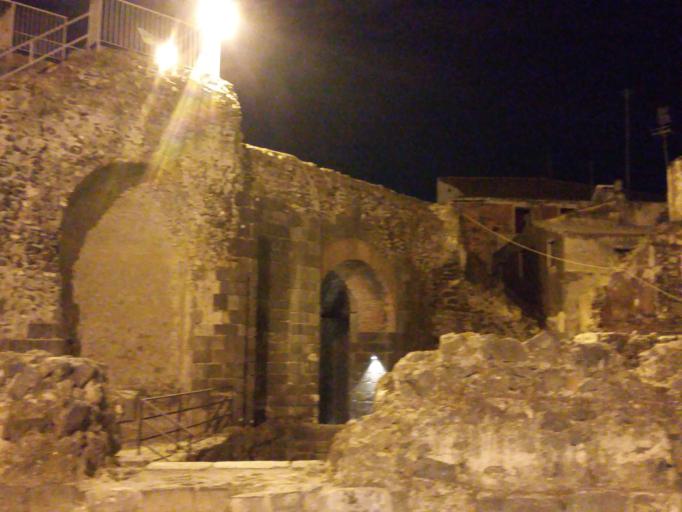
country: IT
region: Sicily
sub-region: Catania
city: Catania
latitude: 37.5031
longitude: 15.0832
